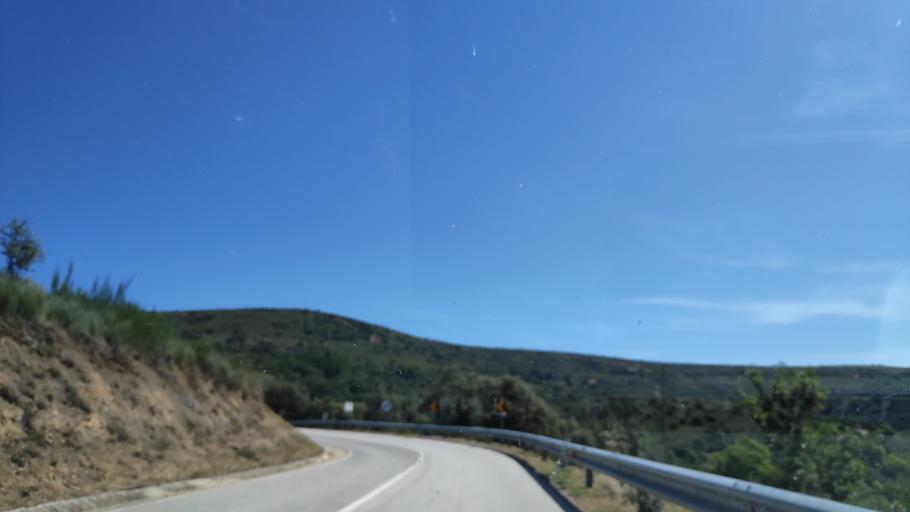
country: PT
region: Braganca
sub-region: Braganca Municipality
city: Braganca
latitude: 41.9076
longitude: -6.7289
